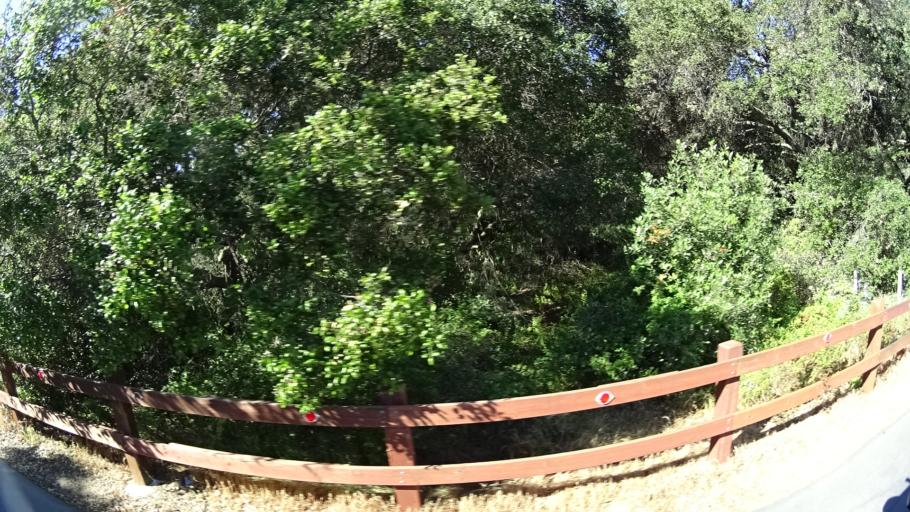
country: US
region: California
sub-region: Ventura County
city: Thousand Oaks
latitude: 34.1757
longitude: -118.8863
